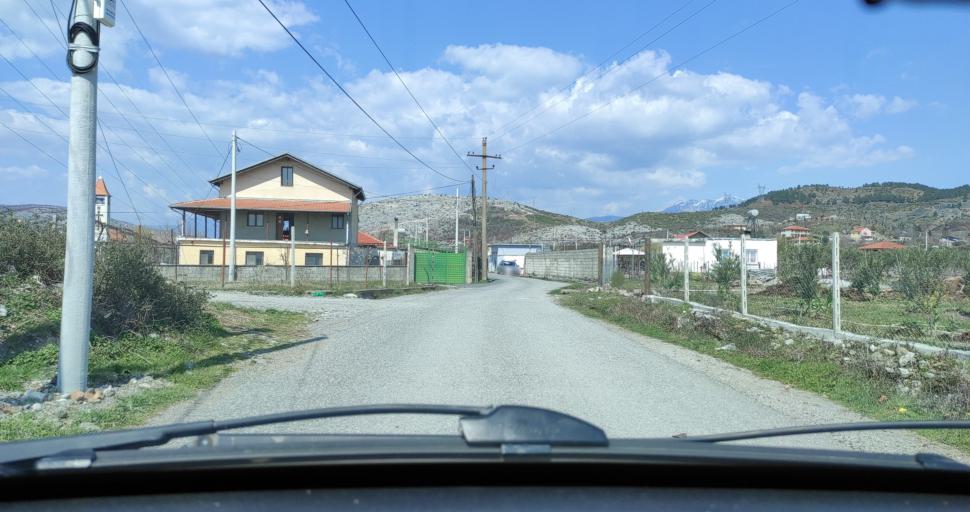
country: AL
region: Shkoder
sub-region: Rrethi i Shkodres
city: Vau i Dejes
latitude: 42.0047
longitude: 19.6419
